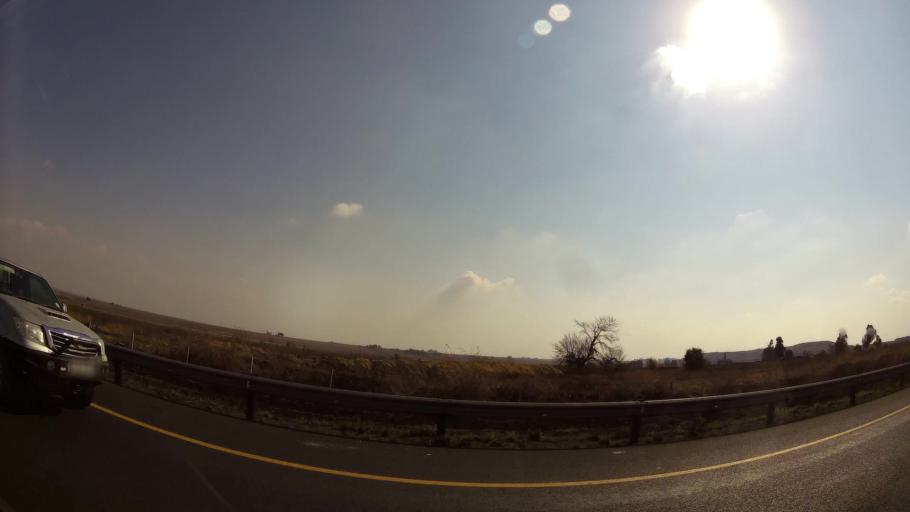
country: ZA
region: Gauteng
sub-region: Ekurhuleni Metropolitan Municipality
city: Springs
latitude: -26.1616
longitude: 28.5169
